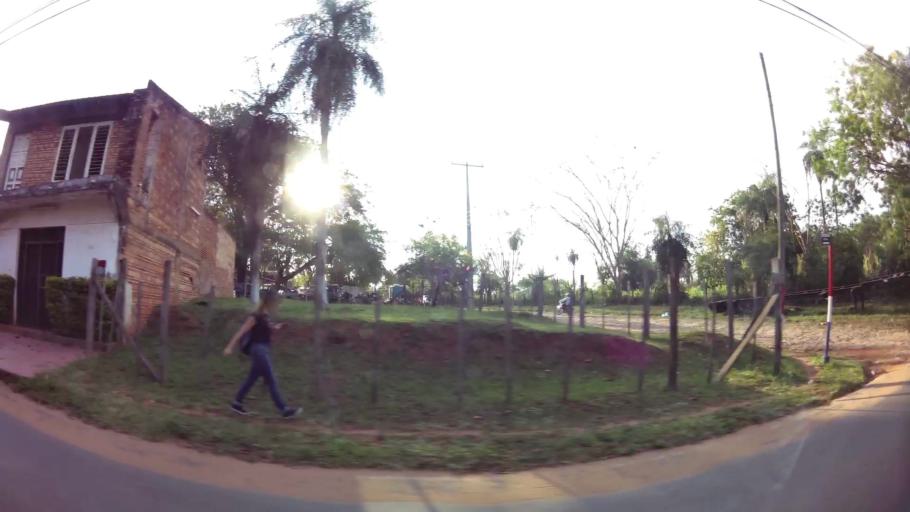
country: PY
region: Central
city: Fernando de la Mora
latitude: -25.3550
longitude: -57.5283
